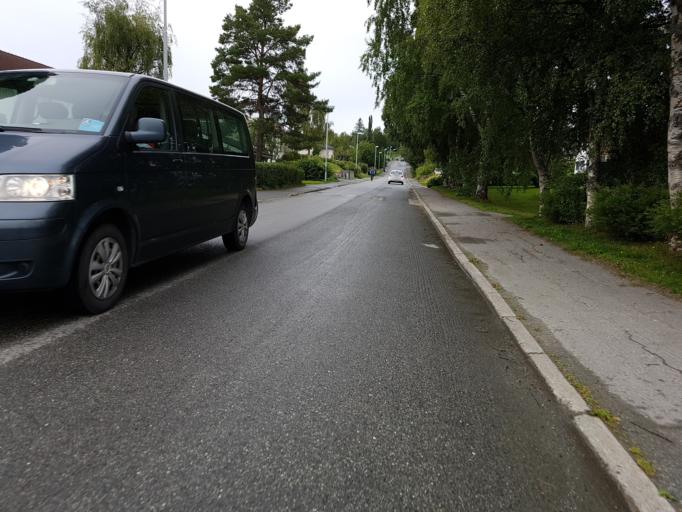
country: NO
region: Sor-Trondelag
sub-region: Trondheim
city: Trondheim
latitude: 63.4009
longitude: 10.3737
